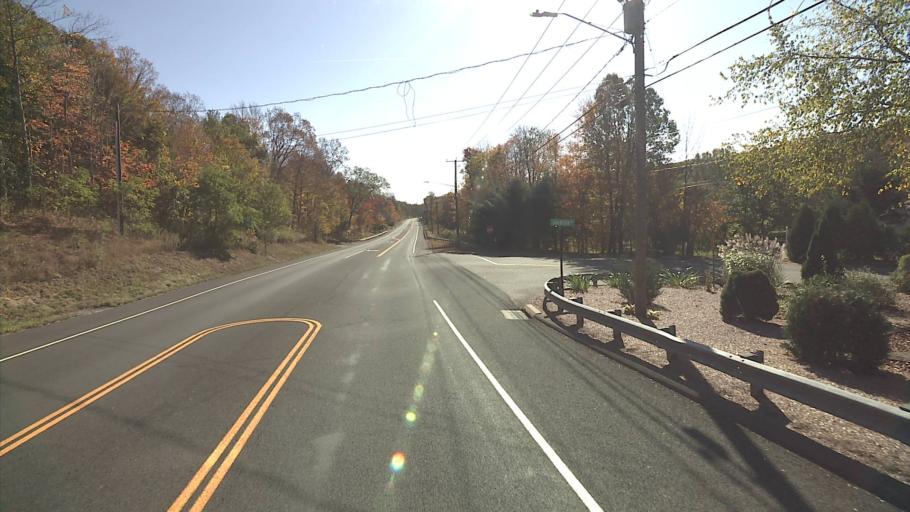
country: US
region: Connecticut
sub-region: Tolland County
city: Rockville
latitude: 41.7819
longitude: -72.4235
